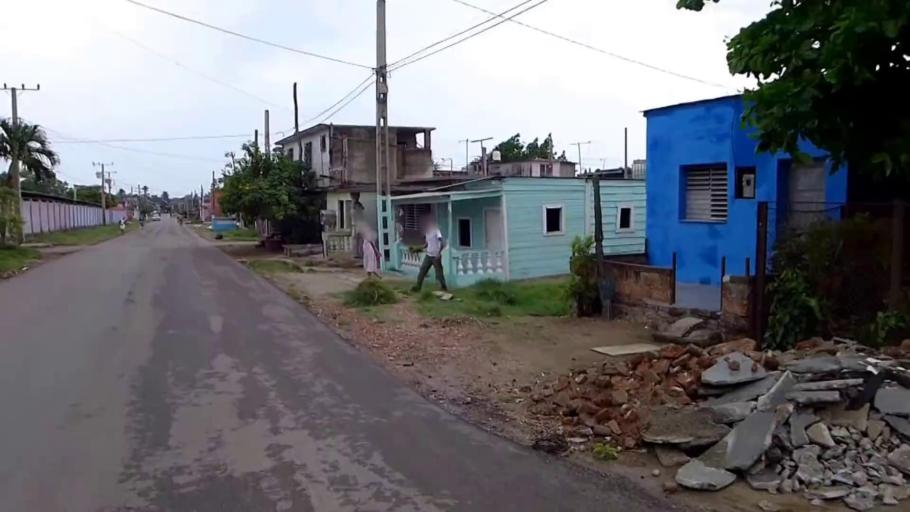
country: CU
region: Camaguey
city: Camaguey
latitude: 21.3903
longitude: -77.9374
